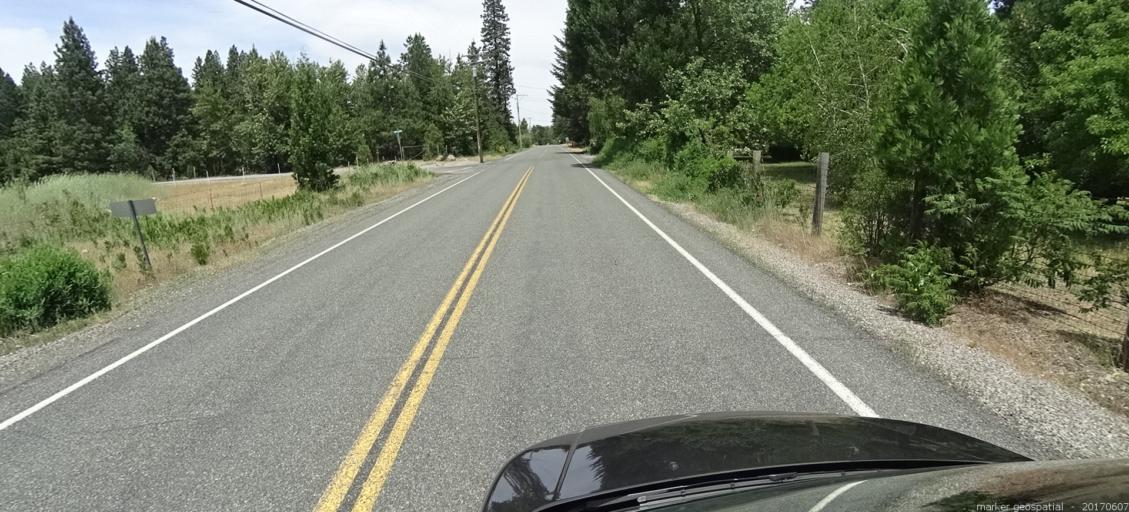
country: US
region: California
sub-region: Siskiyou County
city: Mount Shasta
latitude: 41.2936
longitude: -122.3224
